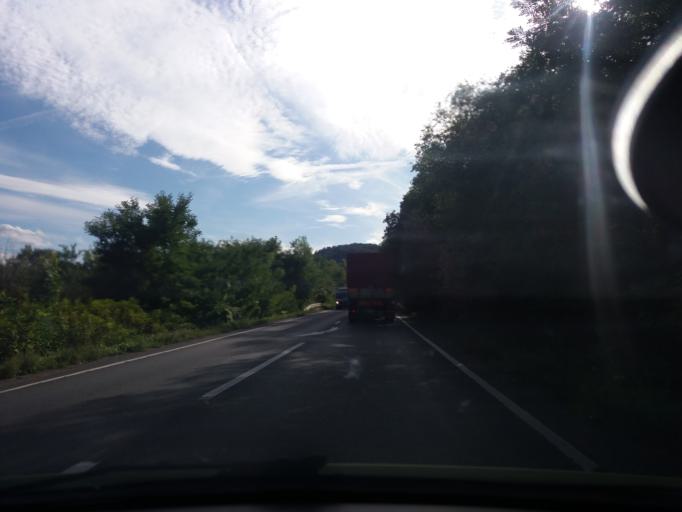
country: RO
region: Arad
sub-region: Oras Lipova
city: Lipova
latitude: 46.1059
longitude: 21.7572
